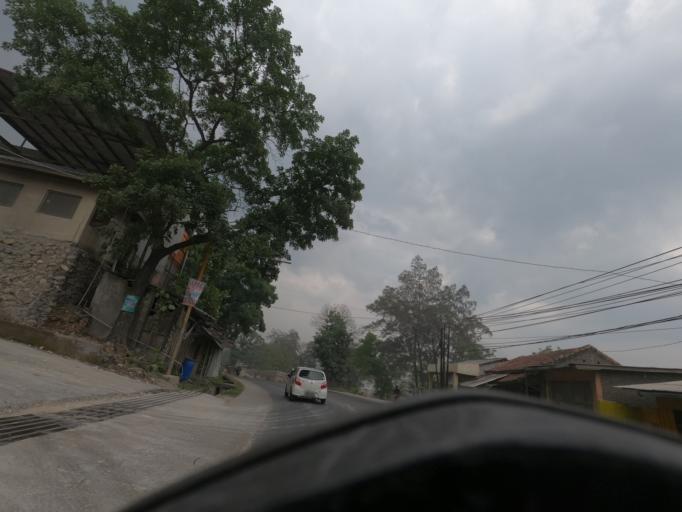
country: ID
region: West Java
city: Padalarang
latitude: -6.8313
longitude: 107.4496
